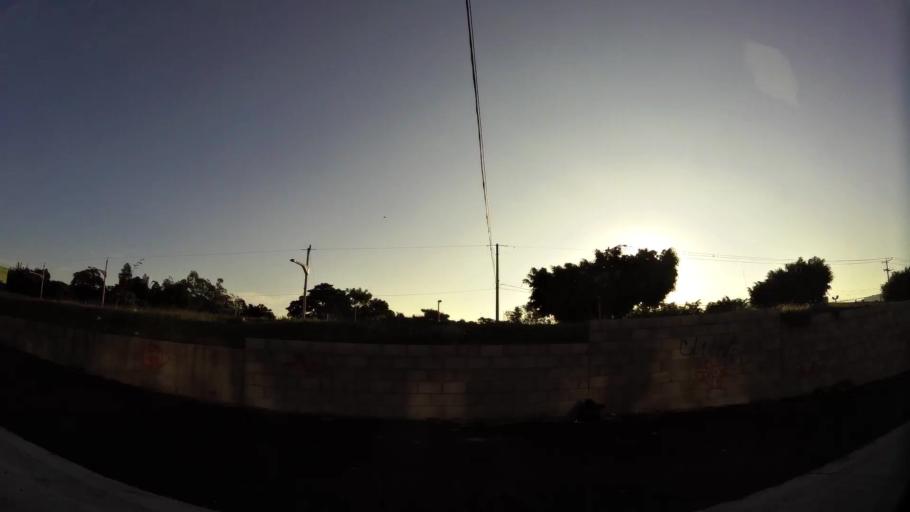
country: SV
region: La Libertad
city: Santa Tecla
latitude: 13.6814
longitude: -89.2636
